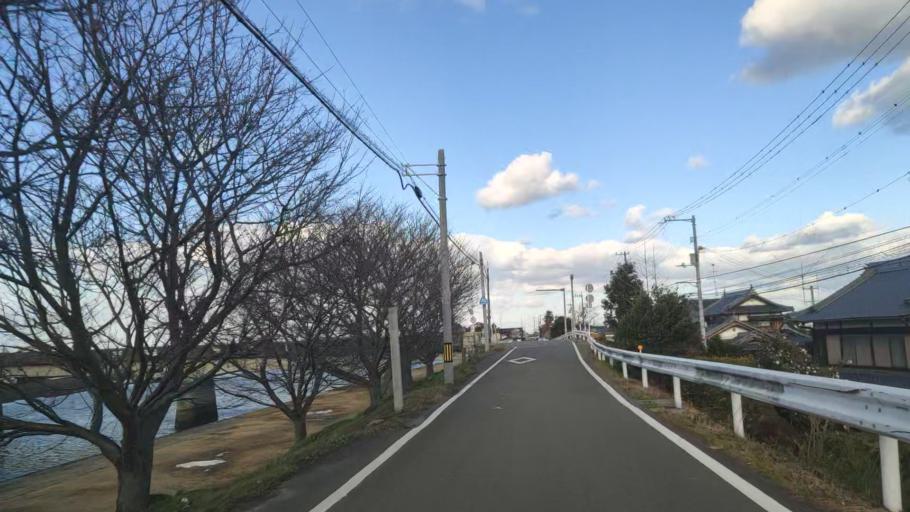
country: JP
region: Ehime
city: Saijo
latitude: 33.9075
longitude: 133.1294
